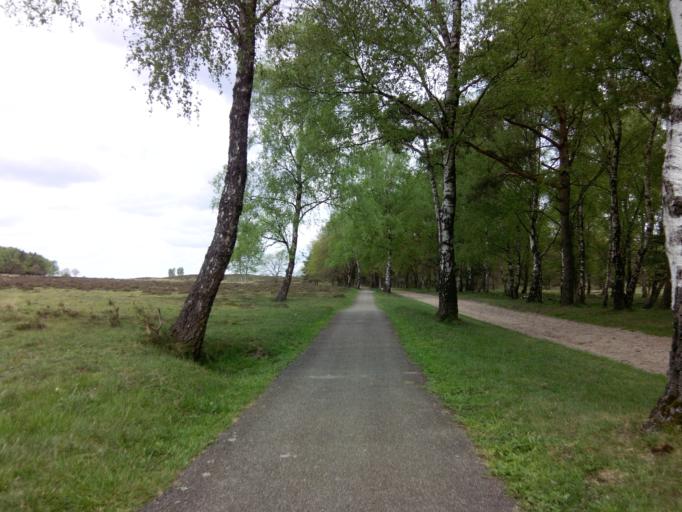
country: NL
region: Gelderland
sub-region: Gemeente Ede
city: Otterlo
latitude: 52.0676
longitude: 5.7587
